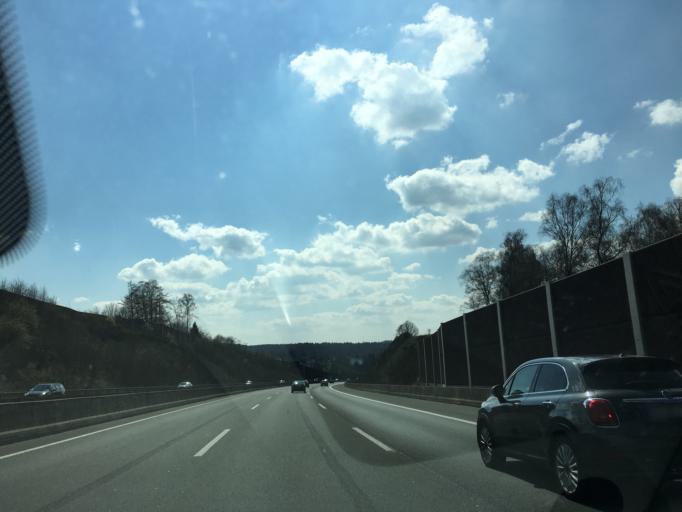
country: DE
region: North Rhine-Westphalia
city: Wermelskirchen
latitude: 51.1741
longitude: 7.2382
